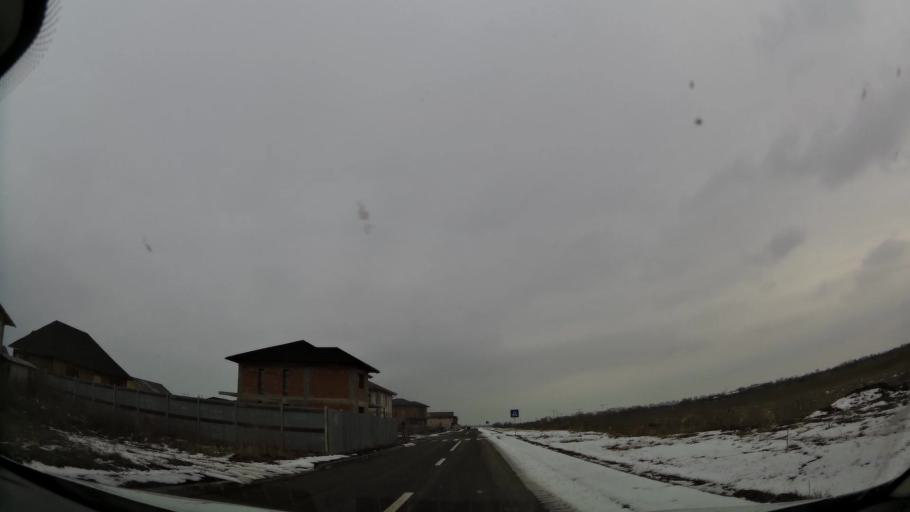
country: RO
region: Ilfov
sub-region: Comuna Tunari
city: Tunari
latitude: 44.5512
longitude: 26.1541
